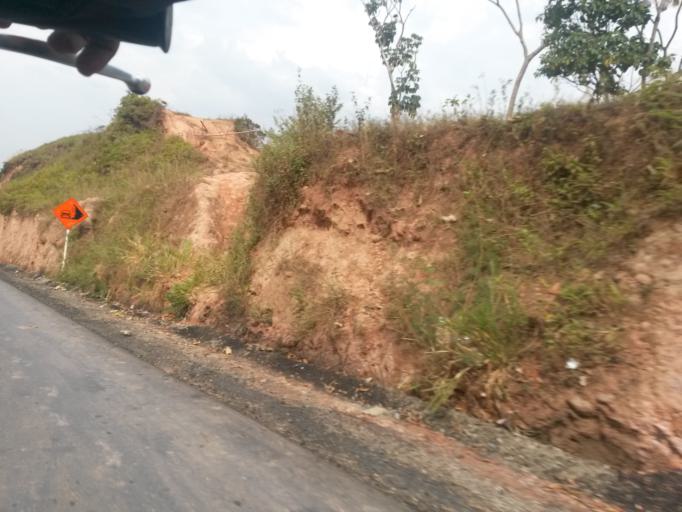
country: CO
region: Cauca
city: Buenos Aires
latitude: 3.0511
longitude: -76.6372
